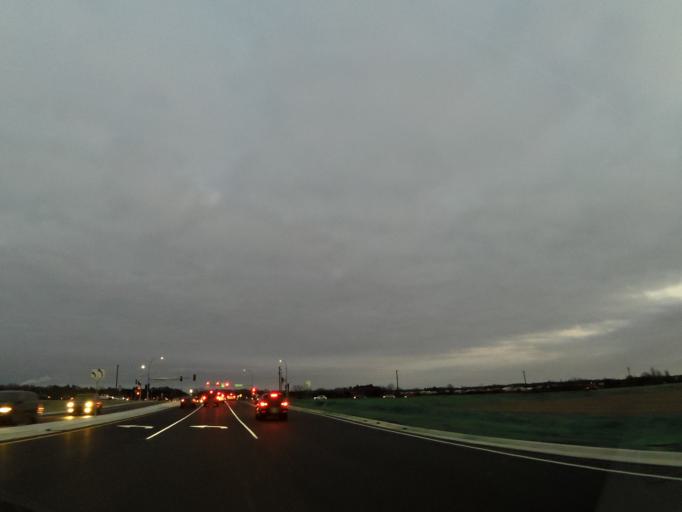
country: US
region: Minnesota
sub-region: Washington County
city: Lake Elmo
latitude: 45.0065
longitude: -92.8651
